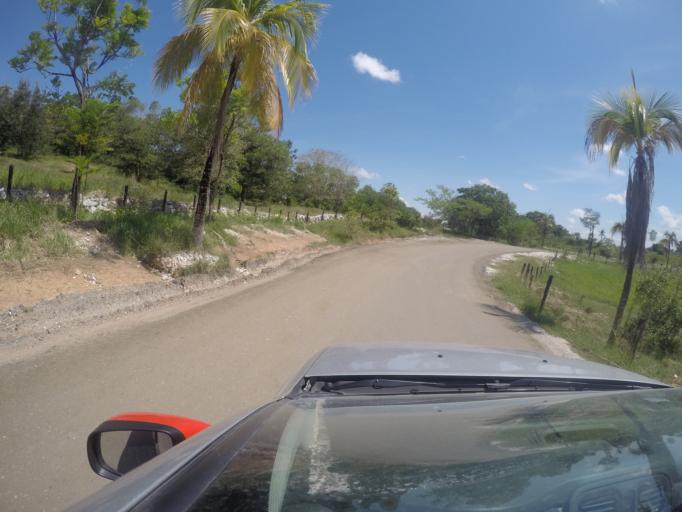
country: CO
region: Antioquia
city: Puerto Triunfo
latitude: 5.9168
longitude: -74.7237
